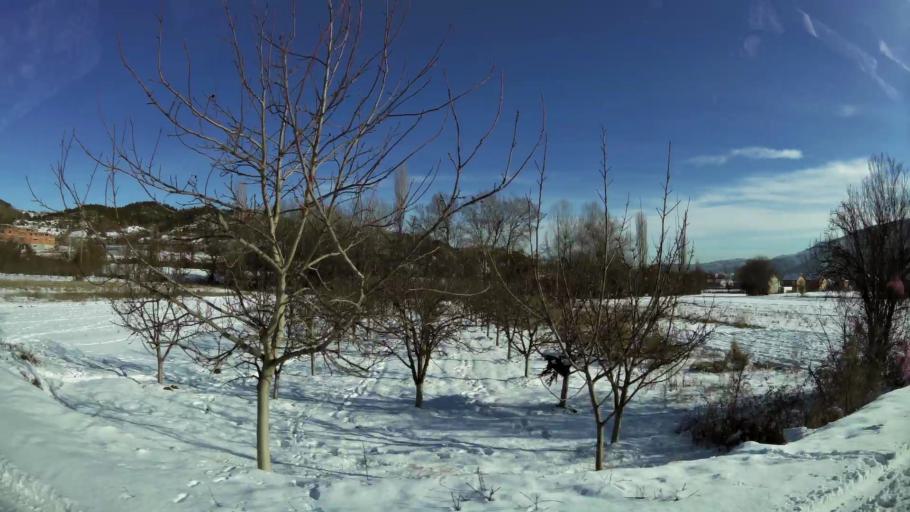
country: MK
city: Ljubin
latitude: 41.9832
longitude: 21.2995
